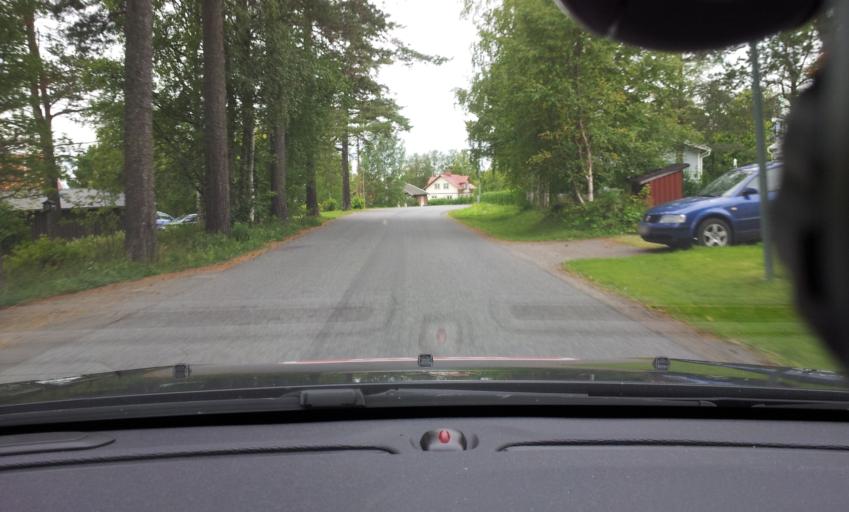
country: SE
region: Jaemtland
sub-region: OEstersunds Kommun
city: Brunflo
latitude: 63.0369
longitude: 14.8798
